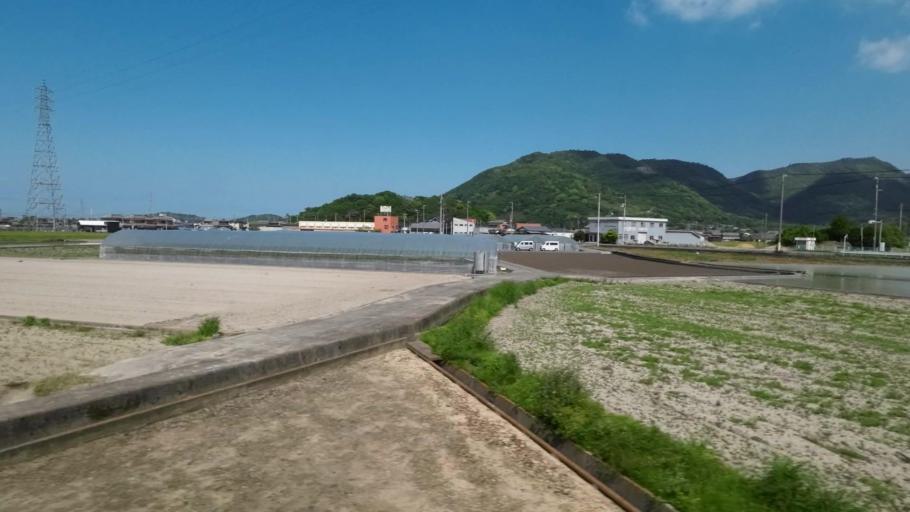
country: JP
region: Kagawa
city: Kan'onjicho
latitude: 34.1347
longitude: 133.6838
